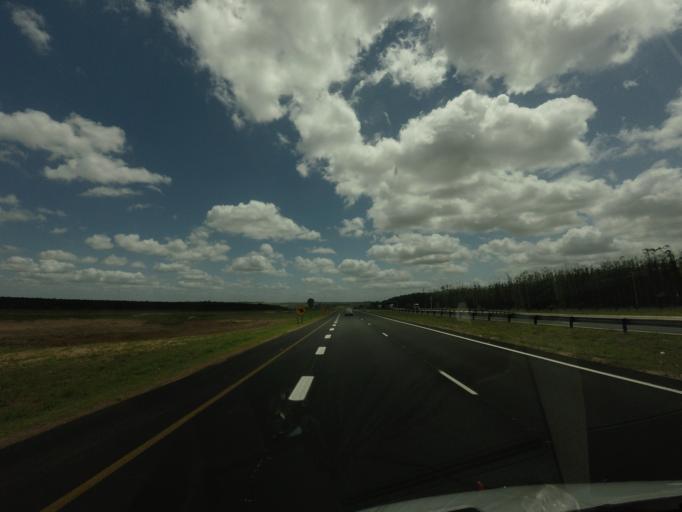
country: ZA
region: KwaZulu-Natal
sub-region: uThungulu District Municipality
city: KwaMbonambi
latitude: -28.5167
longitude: 32.1378
